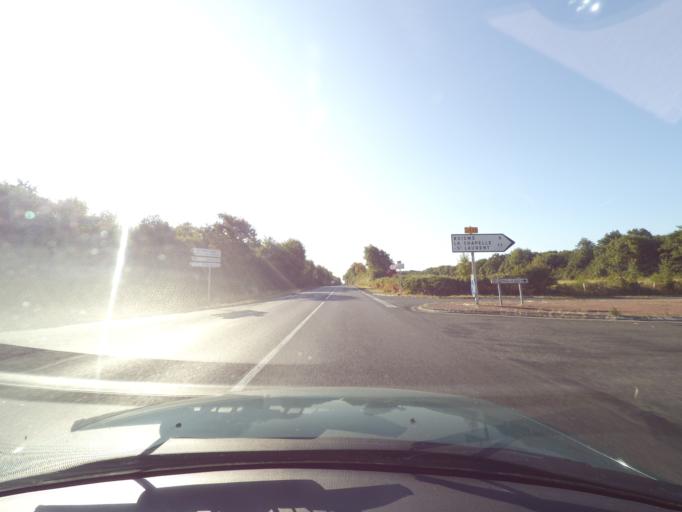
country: FR
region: Poitou-Charentes
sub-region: Departement des Deux-Sevres
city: Chiche
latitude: 46.8153
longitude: -0.3979
